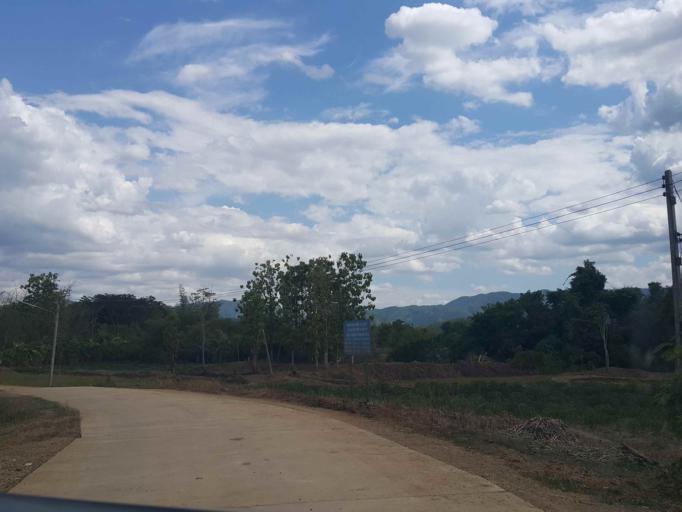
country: TH
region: Sukhothai
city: Thung Saliam
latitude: 17.3270
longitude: 99.4389
